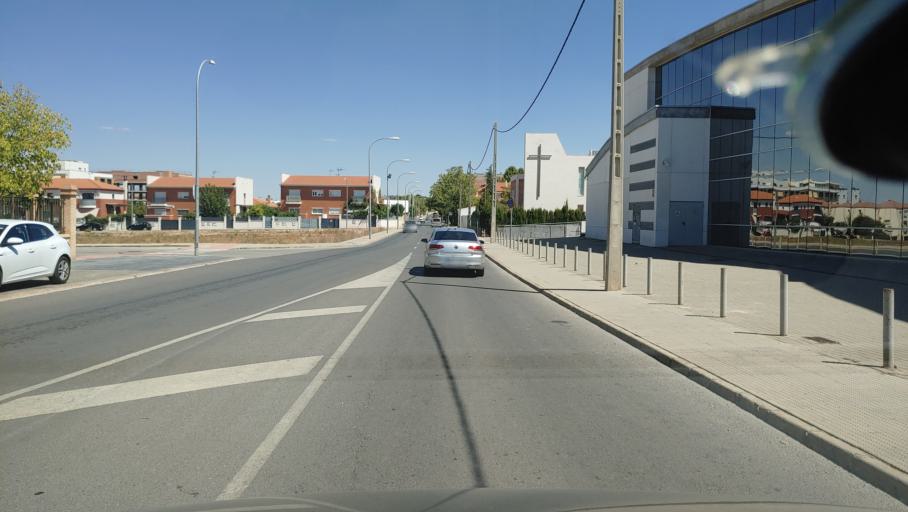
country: ES
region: Castille-La Mancha
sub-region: Provincia de Ciudad Real
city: Valdepenas
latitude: 38.7708
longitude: -3.3863
